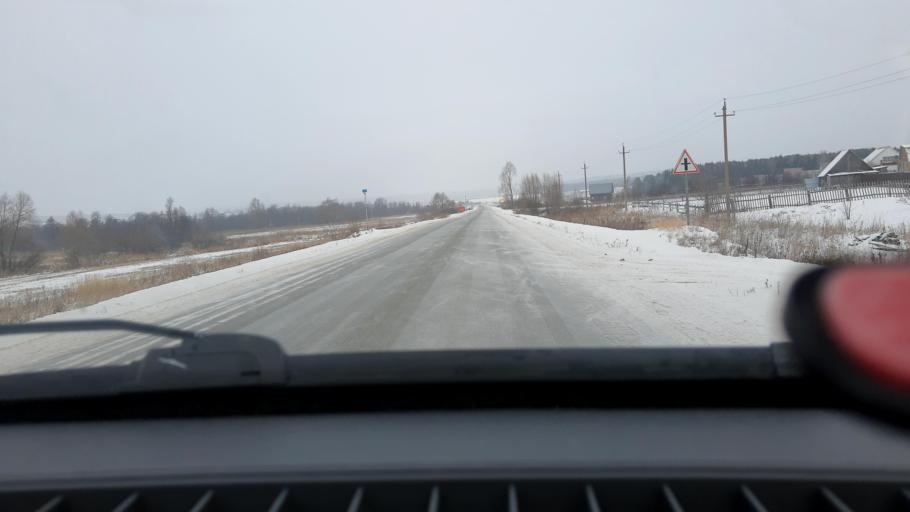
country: RU
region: Bashkortostan
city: Iglino
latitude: 54.7159
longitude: 56.4024
